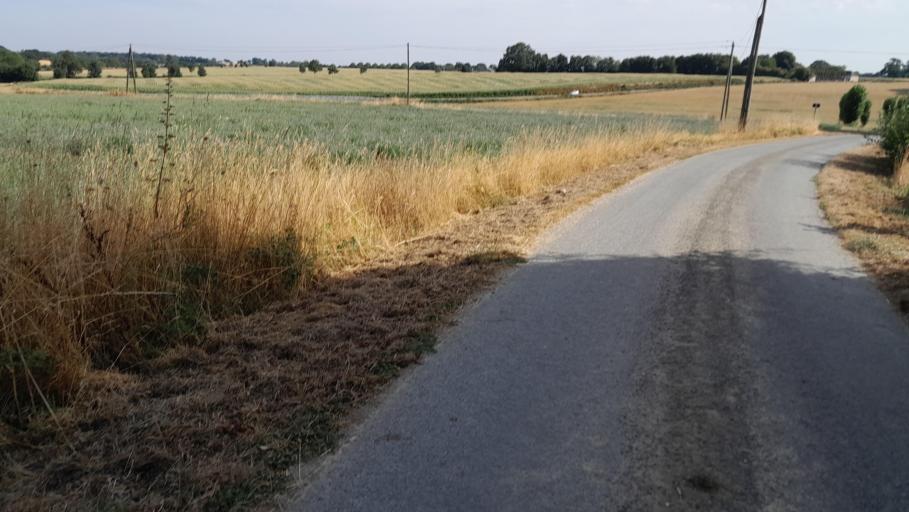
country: FR
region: Pays de la Loire
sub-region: Departement de la Mayenne
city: Ballots
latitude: 47.9587
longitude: -1.0607
